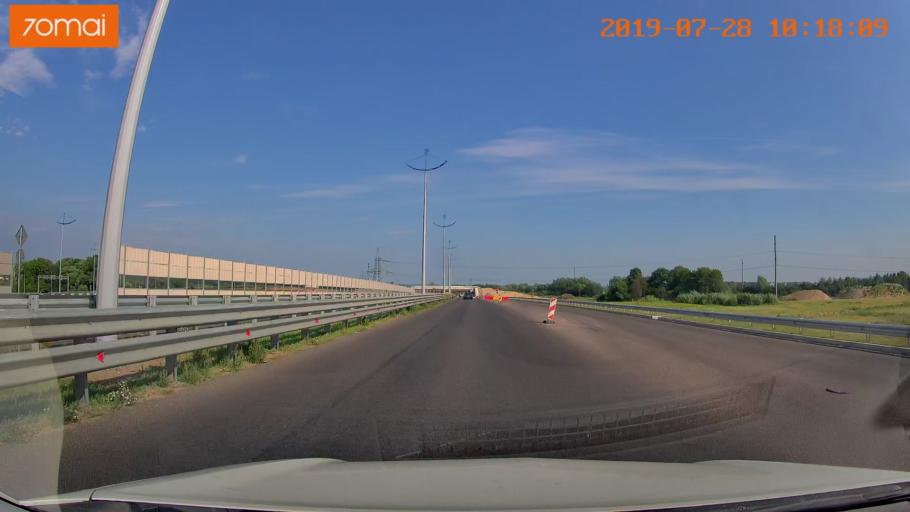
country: RU
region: Kaliningrad
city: Maloye Isakovo
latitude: 54.7484
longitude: 20.5902
